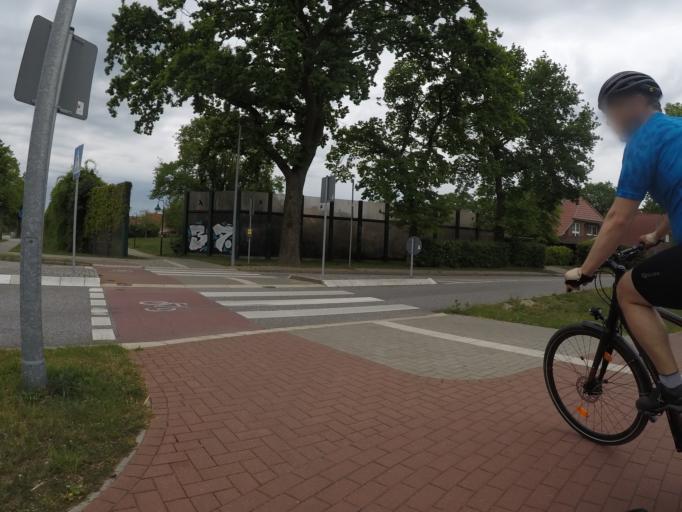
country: DE
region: Schleswig-Holstein
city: Norderstedt
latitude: 53.7020
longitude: 9.9761
